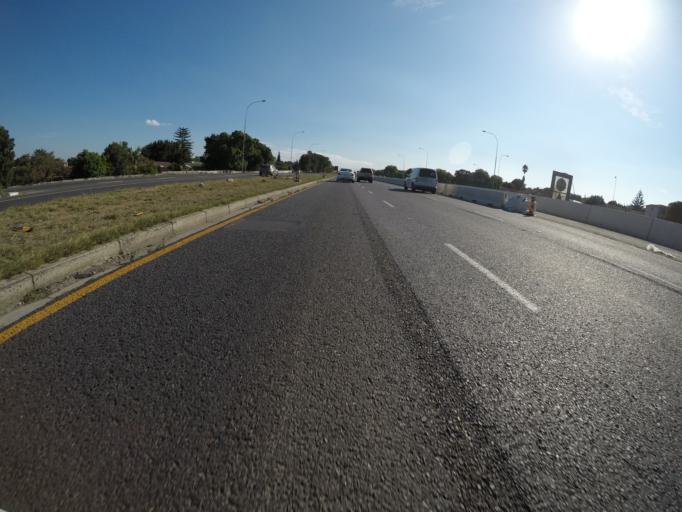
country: ZA
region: Western Cape
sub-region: City of Cape Town
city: Kraaifontein
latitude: -33.8777
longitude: 18.6576
